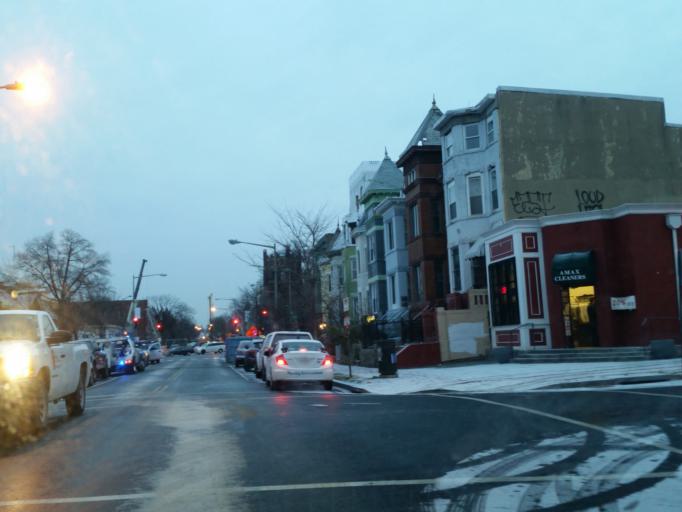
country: US
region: Washington, D.C.
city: Washington, D.C.
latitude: 38.9147
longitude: -77.0121
